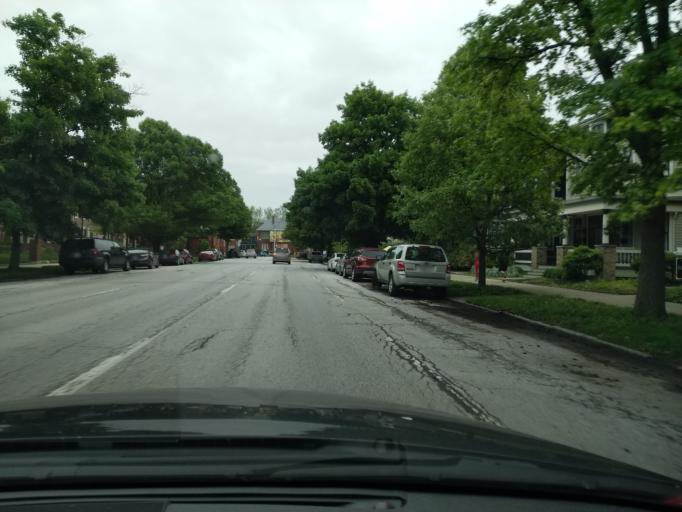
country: US
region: Indiana
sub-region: Marion County
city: Indianapolis
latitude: 39.7871
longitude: -86.1540
